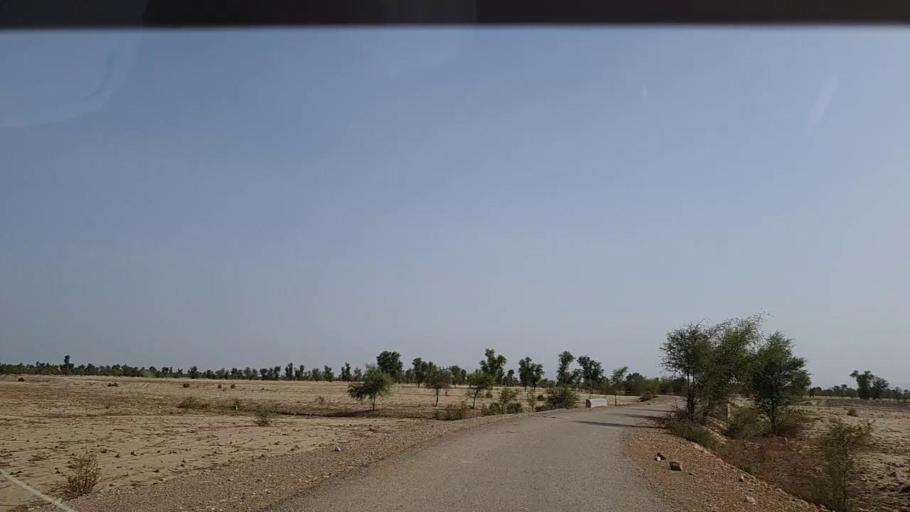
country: PK
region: Sindh
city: Johi
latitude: 26.6343
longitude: 67.5023
